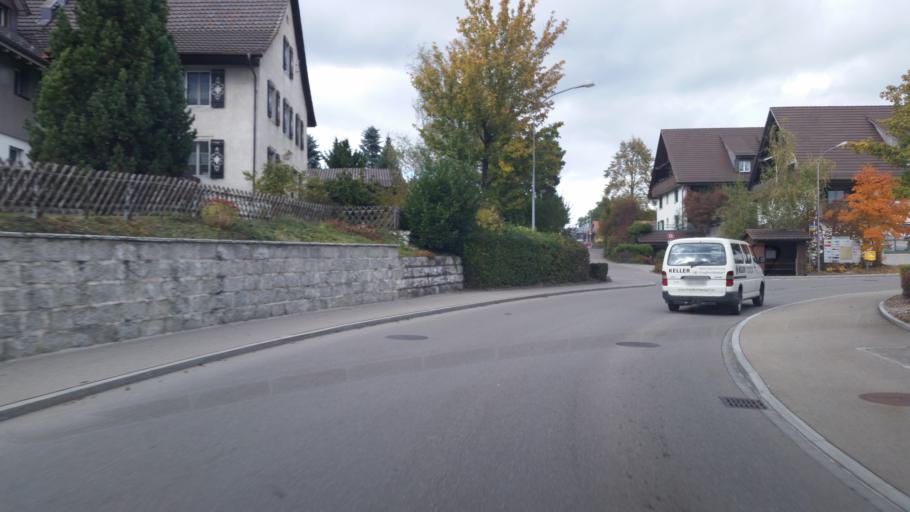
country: CH
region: Zurich
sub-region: Bezirk Dielsdorf
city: Steinmaur
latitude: 47.4984
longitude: 8.4541
